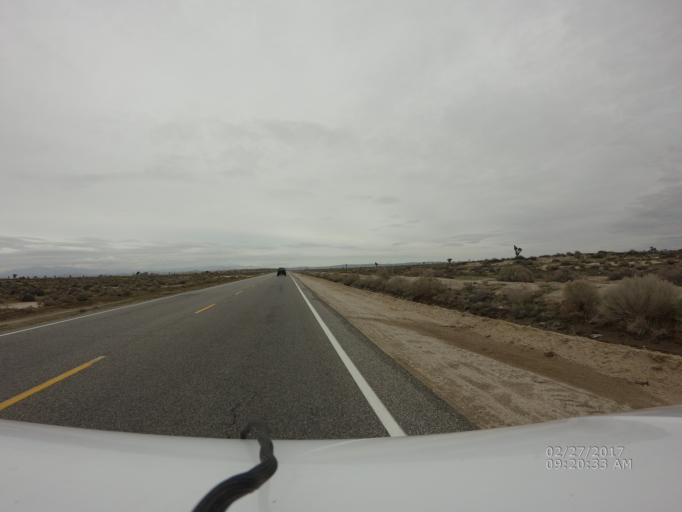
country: US
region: California
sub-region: Los Angeles County
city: Lancaster
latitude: 34.7239
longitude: -118.1125
